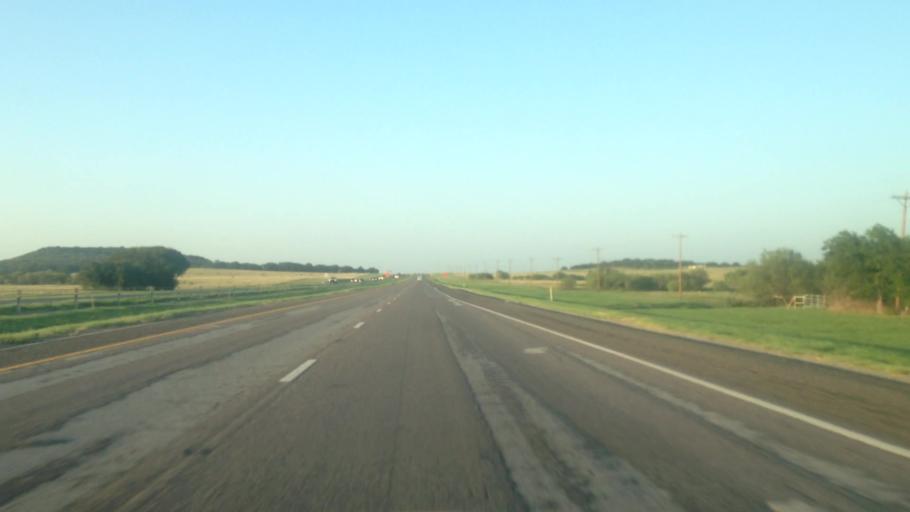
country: US
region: Texas
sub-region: Denton County
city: Argyle
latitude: 33.1363
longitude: -97.2034
